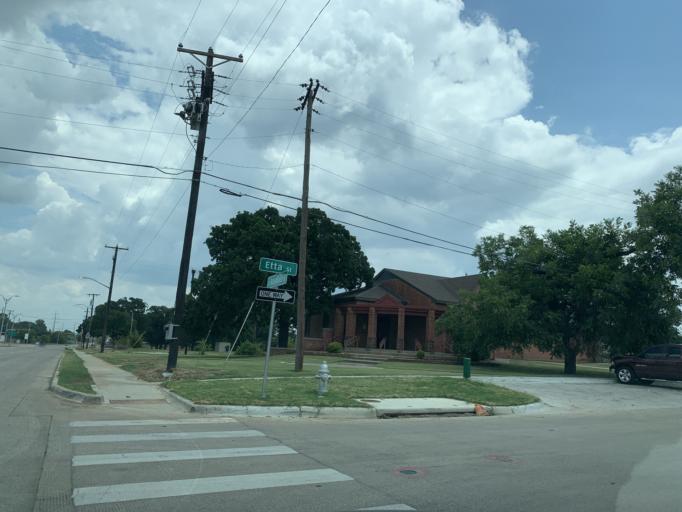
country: US
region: Texas
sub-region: Tarrant County
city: Forest Hill
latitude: 32.7311
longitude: -97.2480
